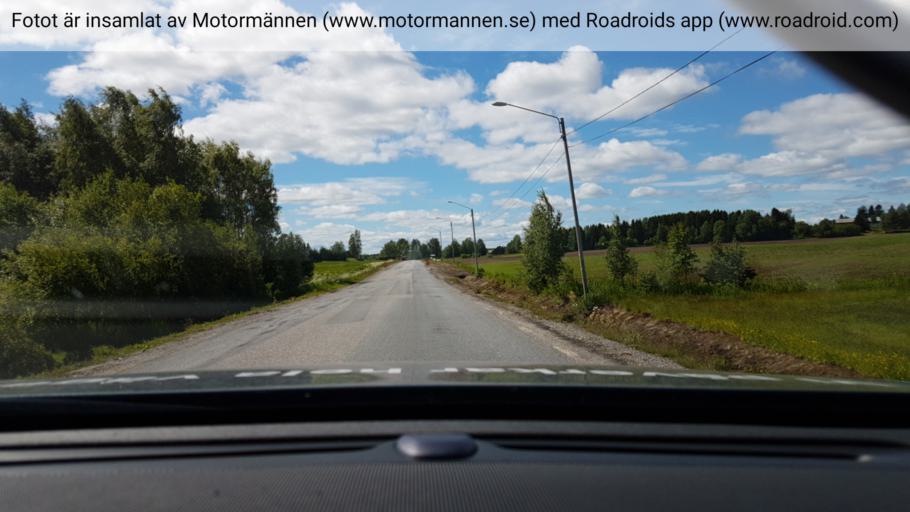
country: SE
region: Vaesterbotten
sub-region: Skelleftea Kommun
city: Burea
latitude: 64.3922
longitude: 21.3259
